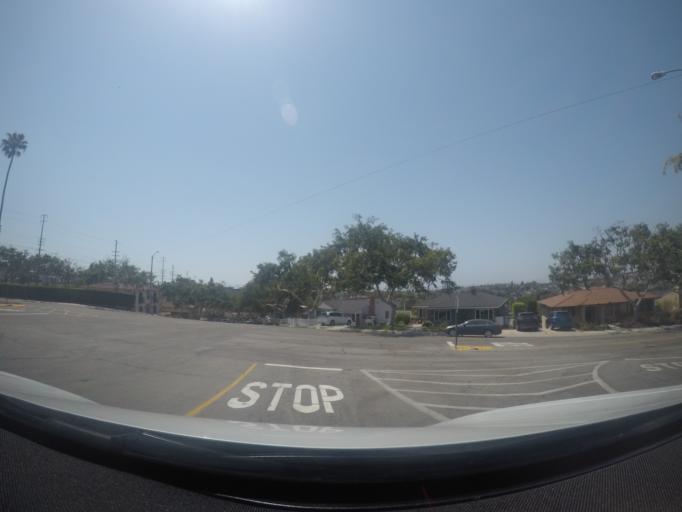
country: US
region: California
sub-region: Los Angeles County
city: Palos Verdes Estates
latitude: 33.8158
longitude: -118.3721
